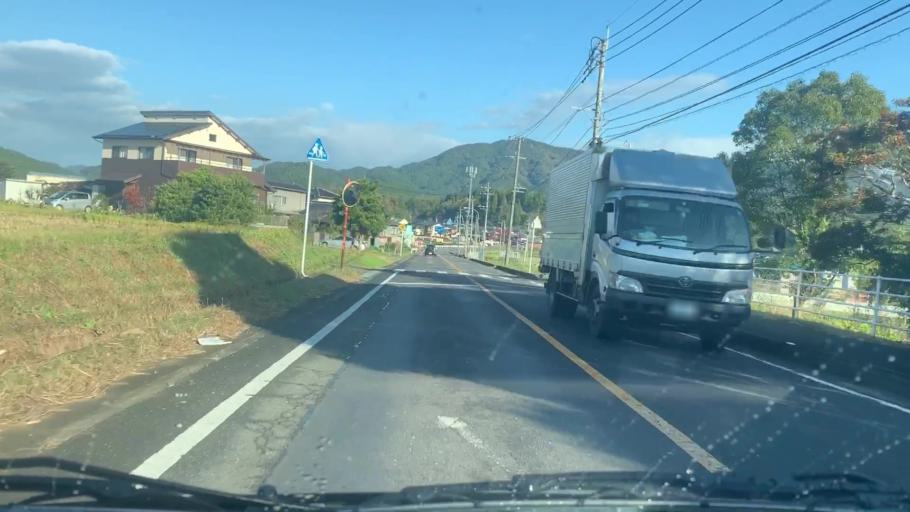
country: JP
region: Saga Prefecture
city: Takeocho-takeo
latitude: 33.2183
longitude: 130.0282
